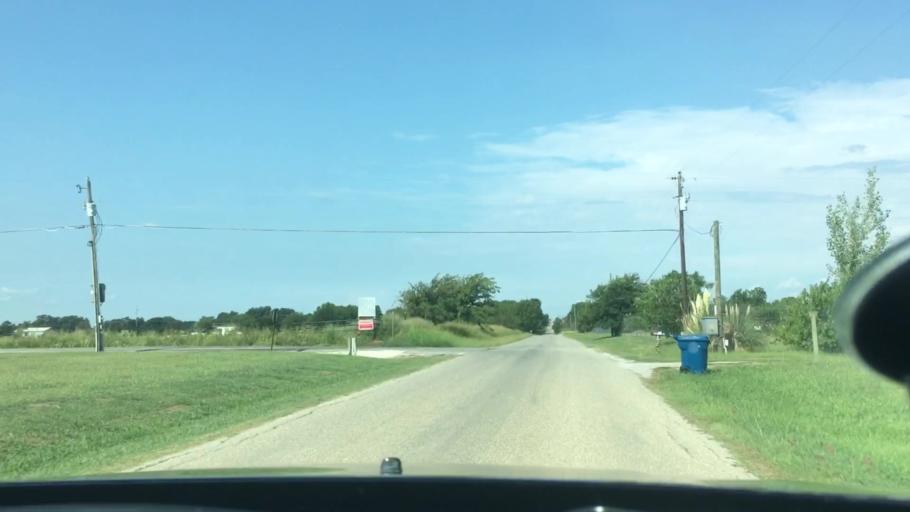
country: US
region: Oklahoma
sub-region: Bryan County
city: Calera
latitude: 33.9110
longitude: -96.4827
